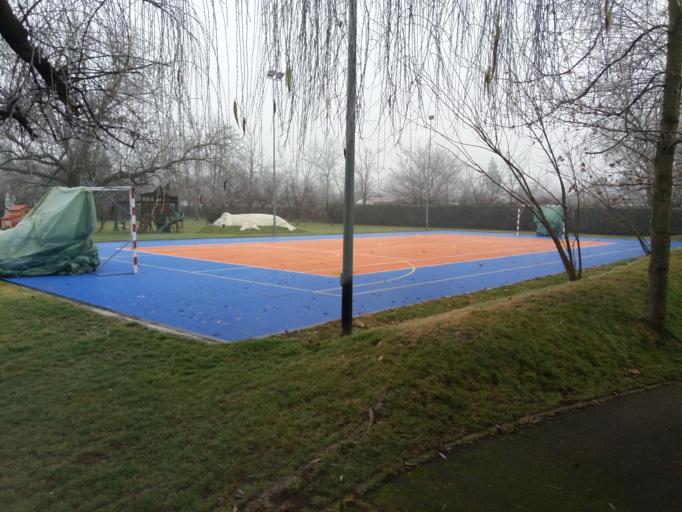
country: RO
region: Giurgiu
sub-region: Comuna Ogrezeni
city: Ogrezeni
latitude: 44.4033
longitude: 25.7818
